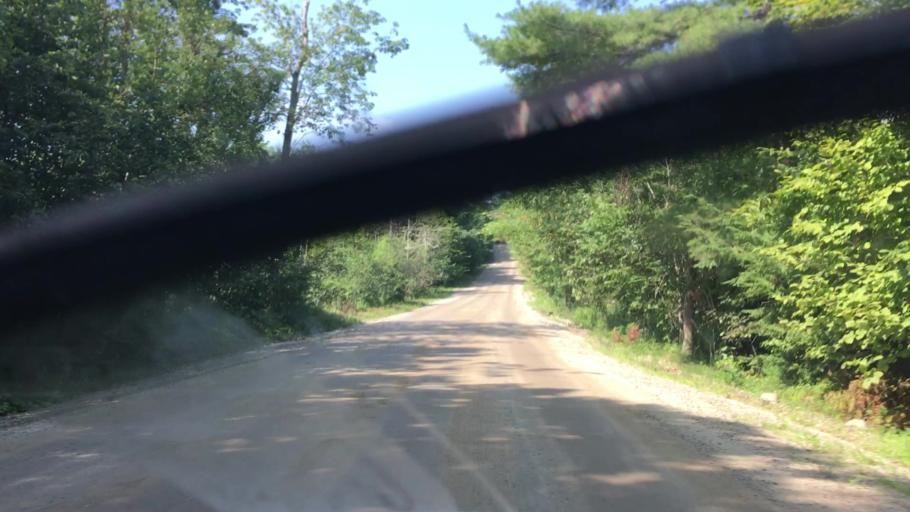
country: US
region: Maine
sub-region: Androscoggin County
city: Poland
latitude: 43.9892
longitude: -70.3766
